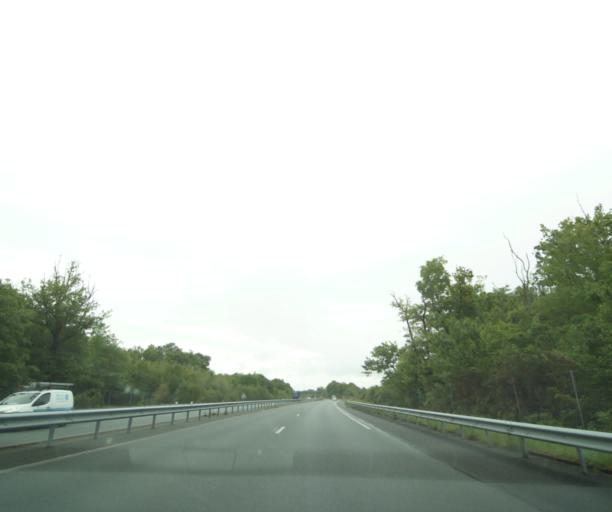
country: FR
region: Poitou-Charentes
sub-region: Departement de la Charente-Maritime
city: Chermignac
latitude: 45.7119
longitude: -0.7003
